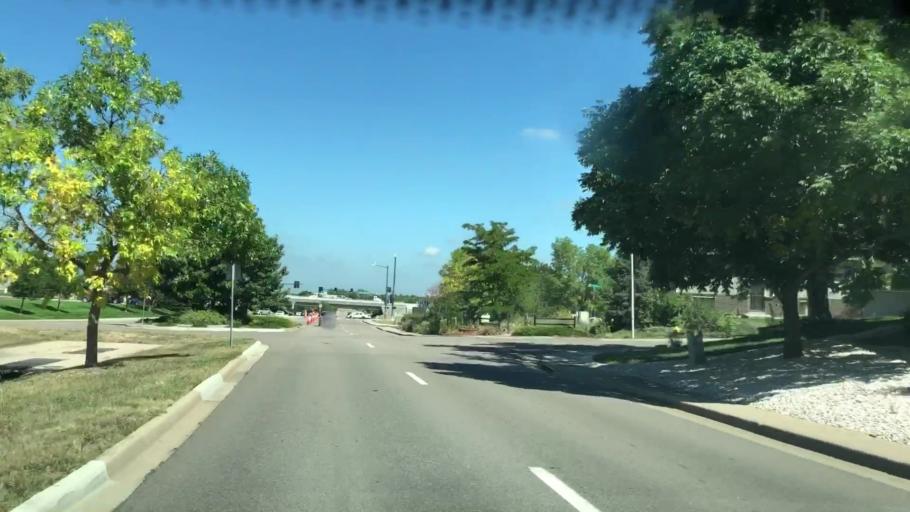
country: US
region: Colorado
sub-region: Douglas County
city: Acres Green
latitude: 39.5613
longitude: -104.8965
